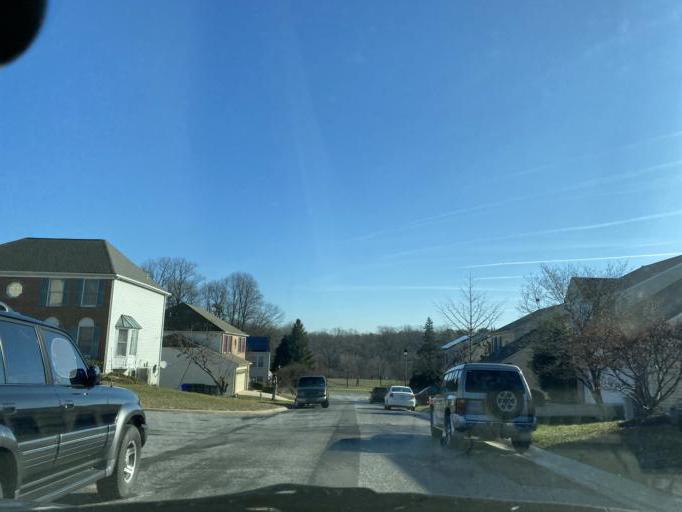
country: US
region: Maryland
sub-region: Montgomery County
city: Burtonsville
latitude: 39.1011
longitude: -76.9192
